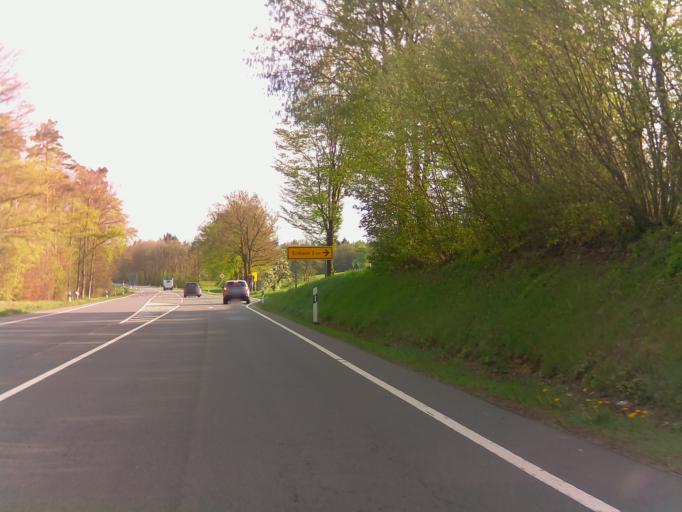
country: DE
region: Baden-Wuerttemberg
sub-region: Karlsruhe Region
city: Limbach
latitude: 49.4864
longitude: 9.2550
